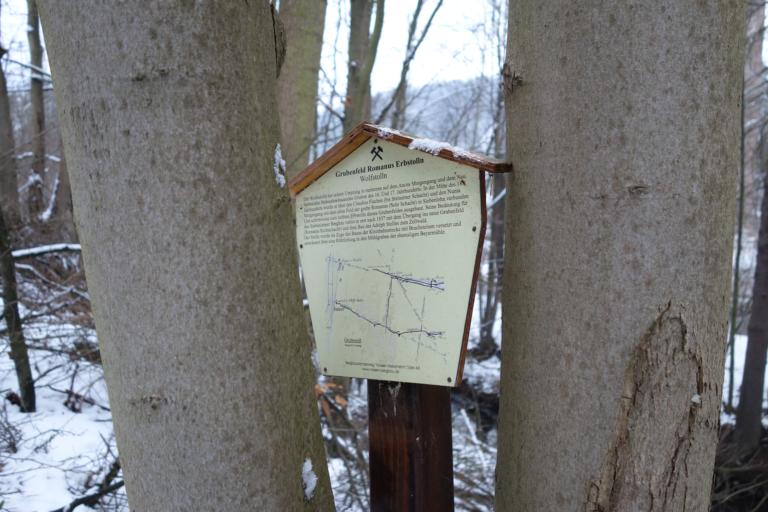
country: DE
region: Saxony
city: Nossen
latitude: 51.0365
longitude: 13.3156
